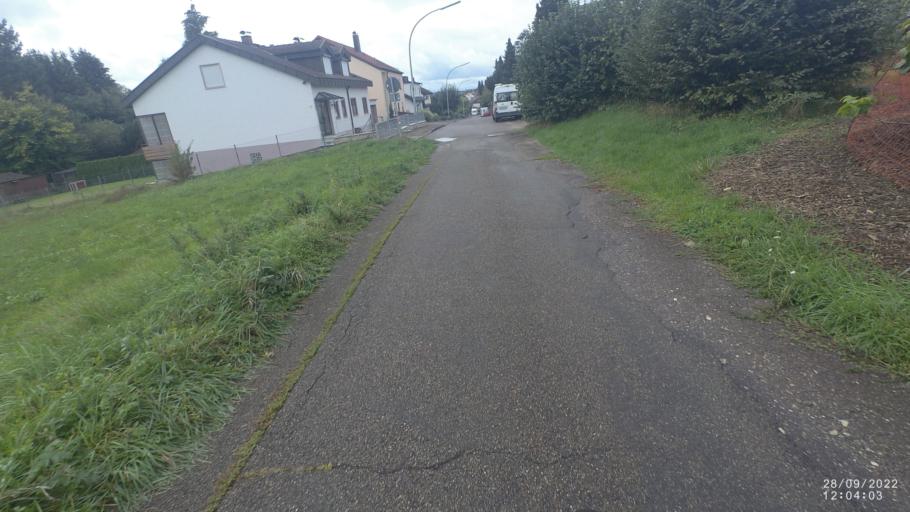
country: DE
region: Baden-Wuerttemberg
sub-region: Regierungsbezirk Stuttgart
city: Wangen
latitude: 48.7291
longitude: 9.6150
